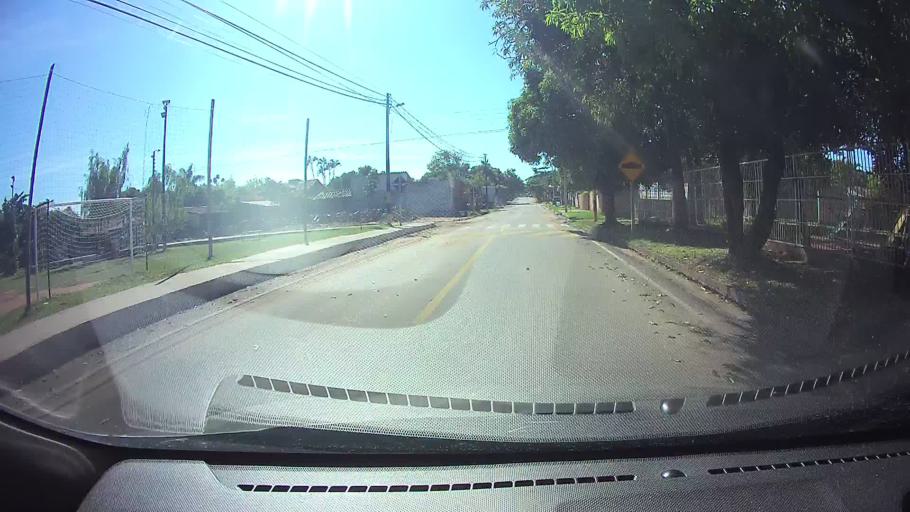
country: PY
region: Central
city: San Lorenzo
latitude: -25.2702
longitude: -57.5084
